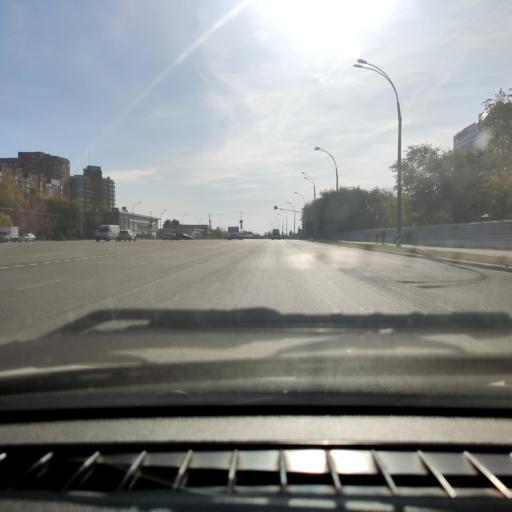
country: RU
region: Samara
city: Tol'yatti
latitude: 53.5040
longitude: 49.2752
